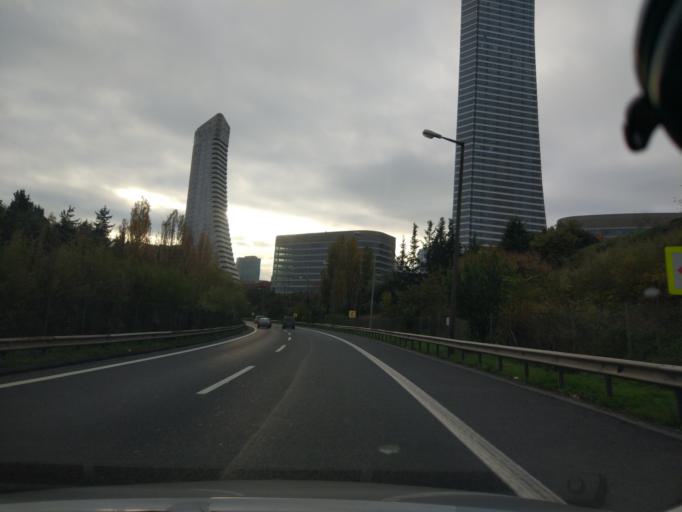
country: TR
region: Istanbul
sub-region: Atasehir
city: Atasehir
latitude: 40.9971
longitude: 29.1204
